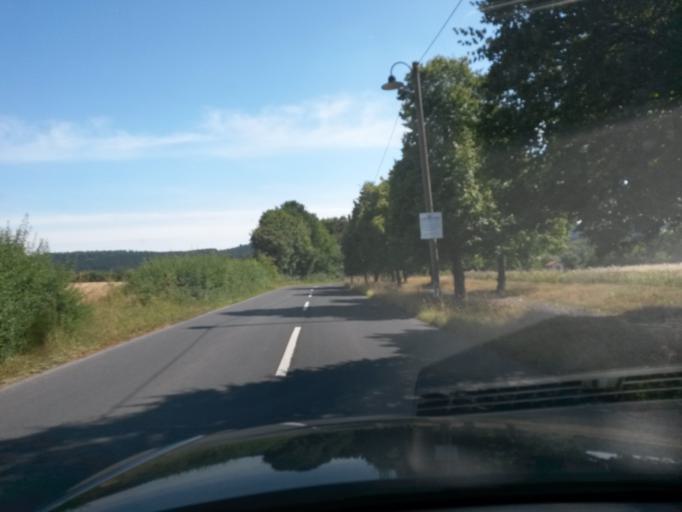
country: DE
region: Hesse
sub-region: Regierungsbezirk Darmstadt
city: Wehrheim
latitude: 50.2795
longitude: 8.5302
